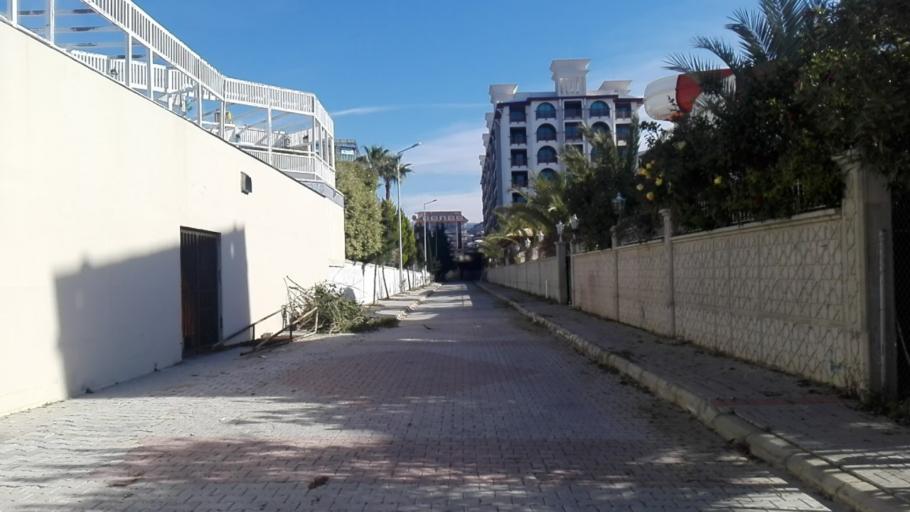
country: TR
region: Antalya
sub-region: Alanya
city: Payallar
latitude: 36.5784
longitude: 31.8848
